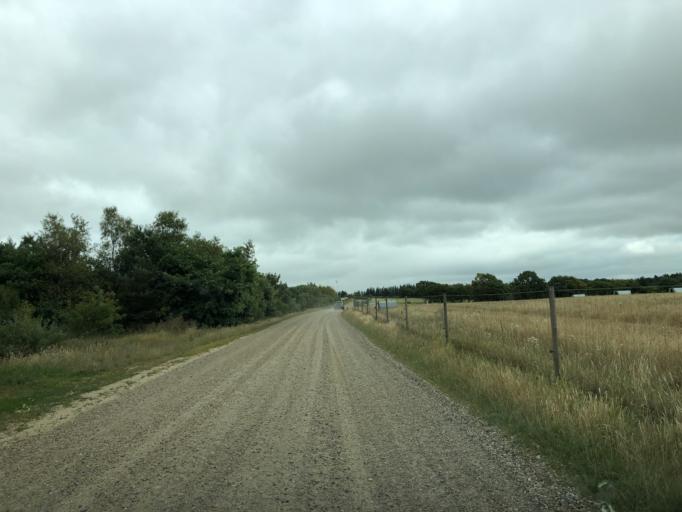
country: DK
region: Central Jutland
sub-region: Holstebro Kommune
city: Holstebro
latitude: 56.2340
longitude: 8.6327
